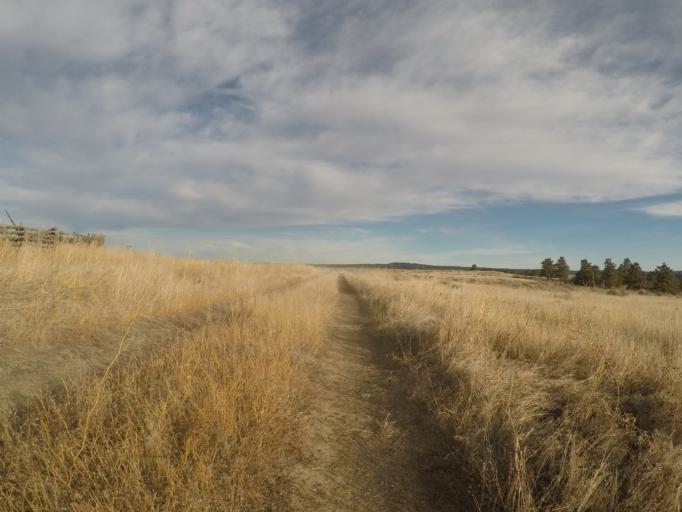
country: US
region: Montana
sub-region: Musselshell County
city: Roundup
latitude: 46.2749
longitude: -108.7656
